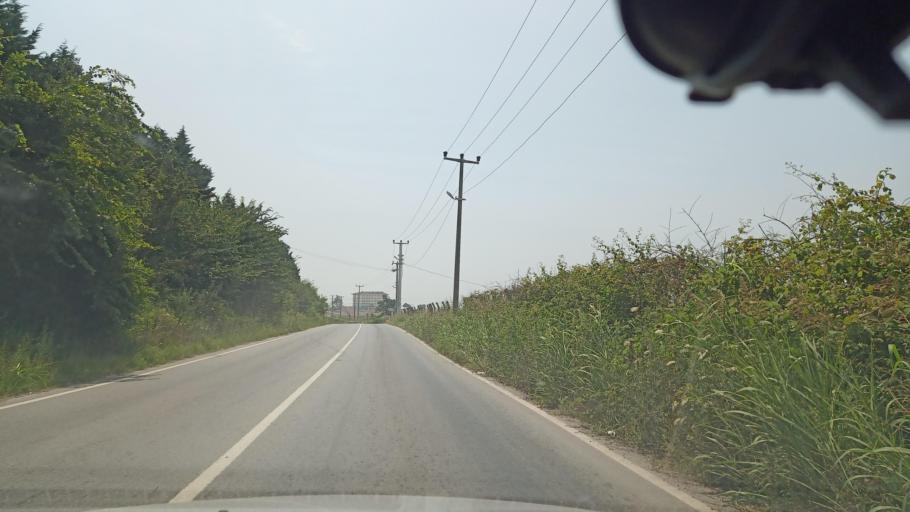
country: TR
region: Sakarya
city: Adapazari
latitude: 40.8300
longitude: 30.3965
